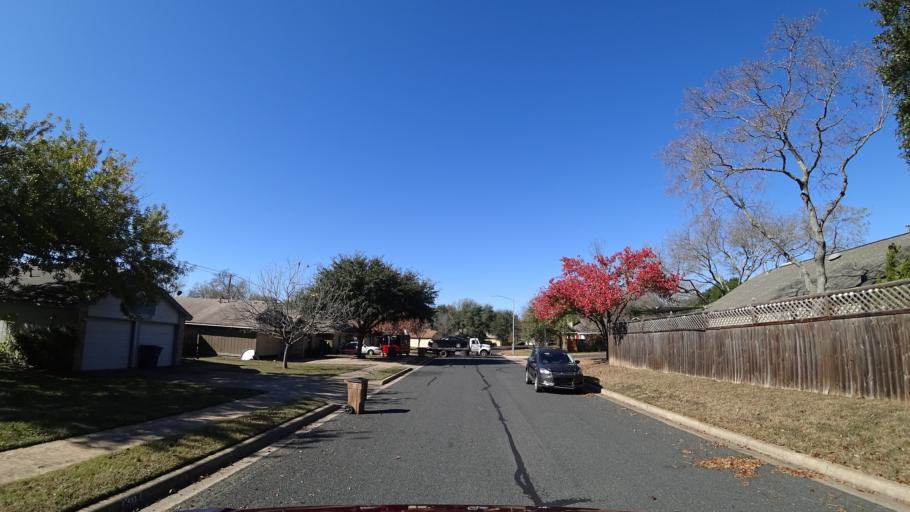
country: US
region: Texas
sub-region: Travis County
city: Wells Branch
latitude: 30.4132
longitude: -97.7022
